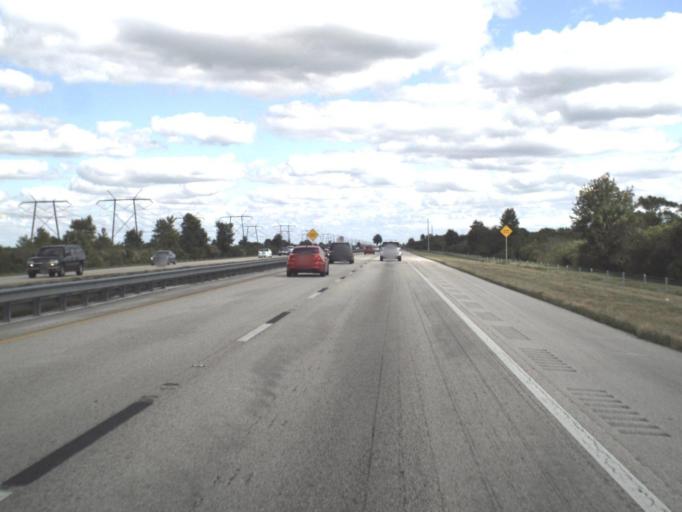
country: US
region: Florida
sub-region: Indian River County
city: Fellsmere
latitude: 27.5593
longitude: -80.7350
